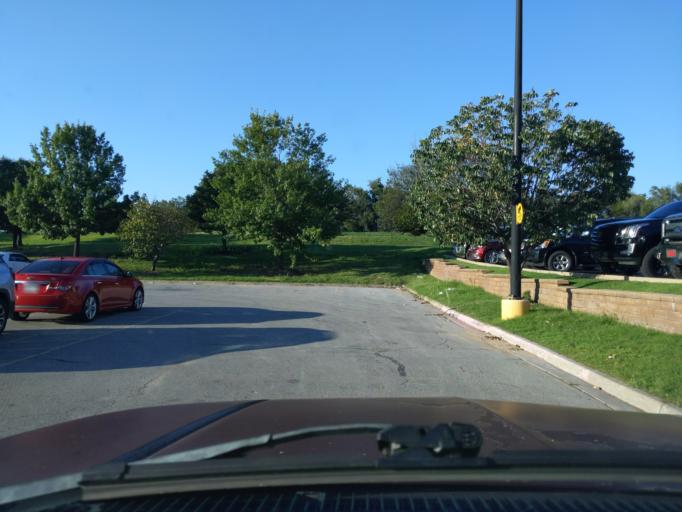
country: US
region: Oklahoma
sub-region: Tulsa County
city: Sand Springs
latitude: 36.1360
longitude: -96.1193
